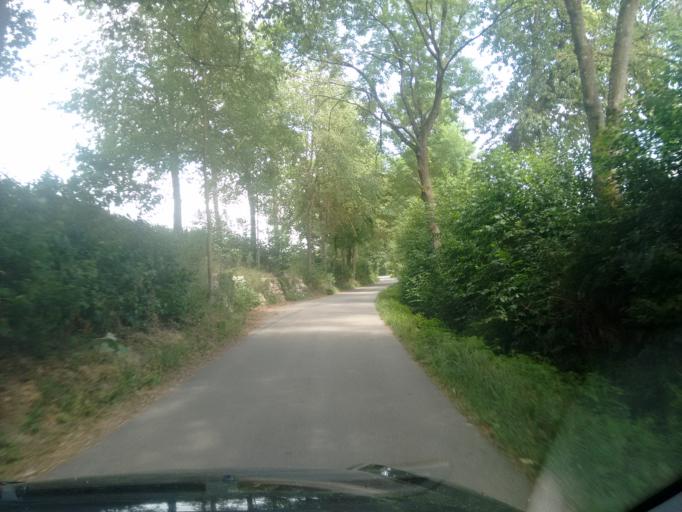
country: AT
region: Upper Austria
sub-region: Wels-Land
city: Gunskirchen
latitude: 48.1666
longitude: 13.9485
